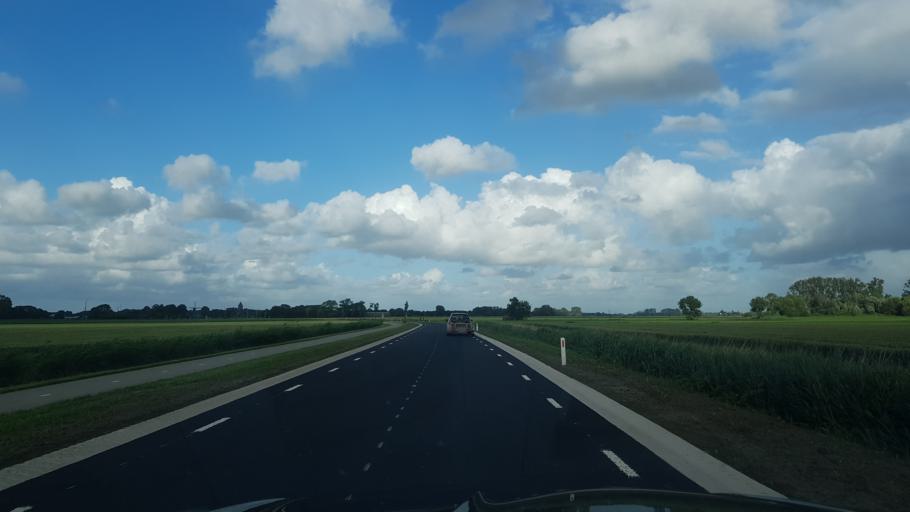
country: NL
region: Groningen
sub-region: Gemeente Bedum
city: Bedum
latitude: 53.3275
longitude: 6.7196
